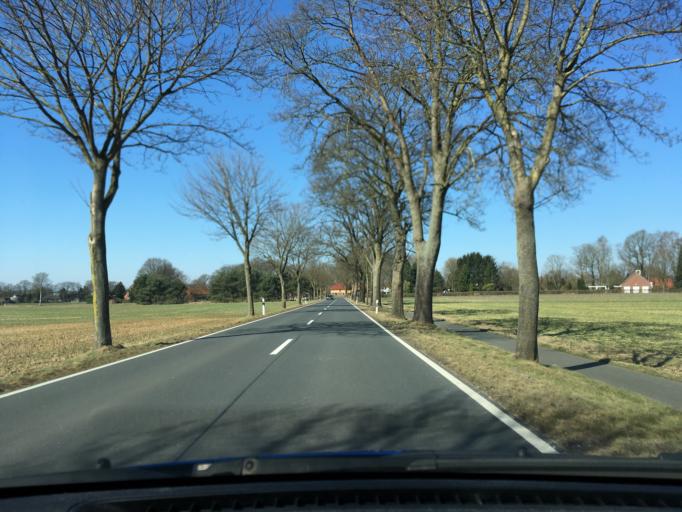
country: DE
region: Lower Saxony
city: Hemslingen
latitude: 53.0772
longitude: 9.6229
